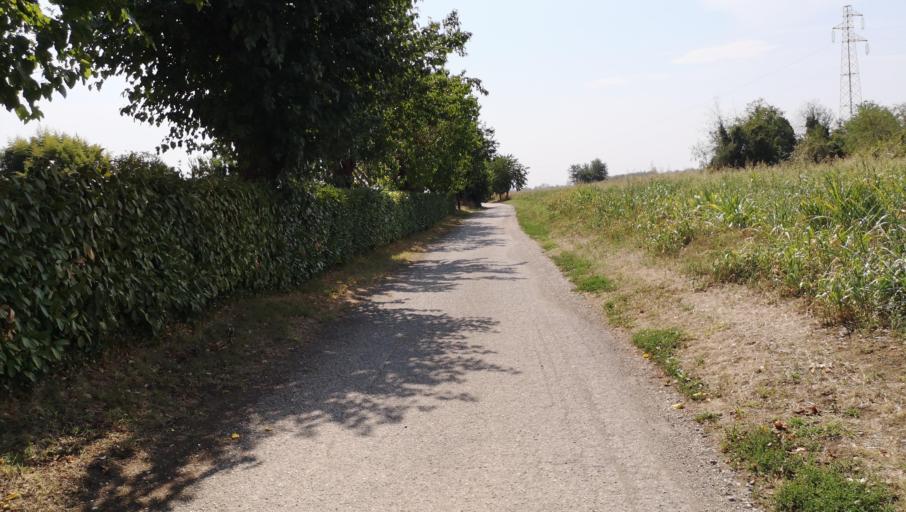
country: IT
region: Friuli Venezia Giulia
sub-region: Provincia di Udine
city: Udine
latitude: 46.0472
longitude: 13.2635
